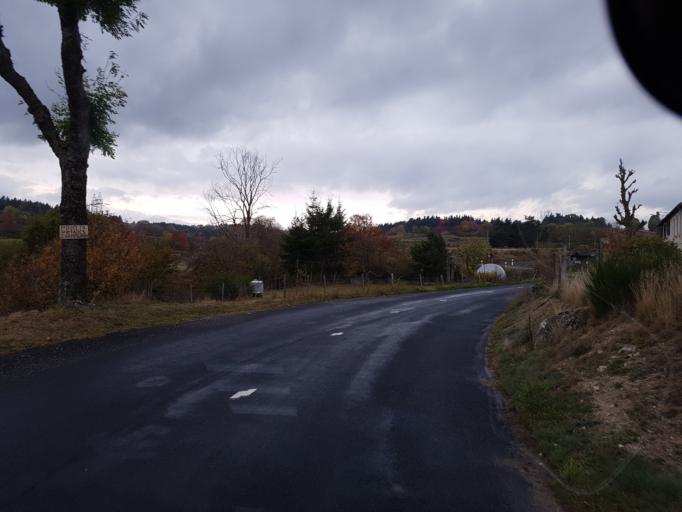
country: FR
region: Languedoc-Roussillon
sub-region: Departement de la Lozere
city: Langogne
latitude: 44.7135
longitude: 3.8058
